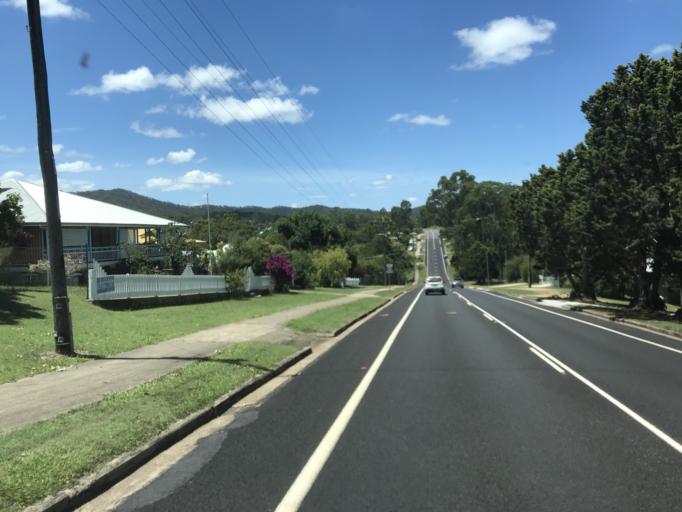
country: AU
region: Queensland
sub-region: Tablelands
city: Atherton
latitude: -17.3903
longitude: 145.3872
